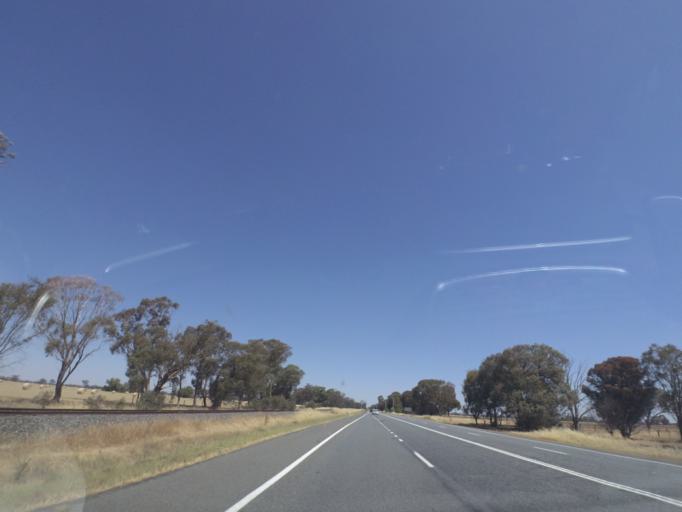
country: AU
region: Victoria
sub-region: Greater Shepparton
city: Shepparton
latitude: -36.1946
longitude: 145.4319
